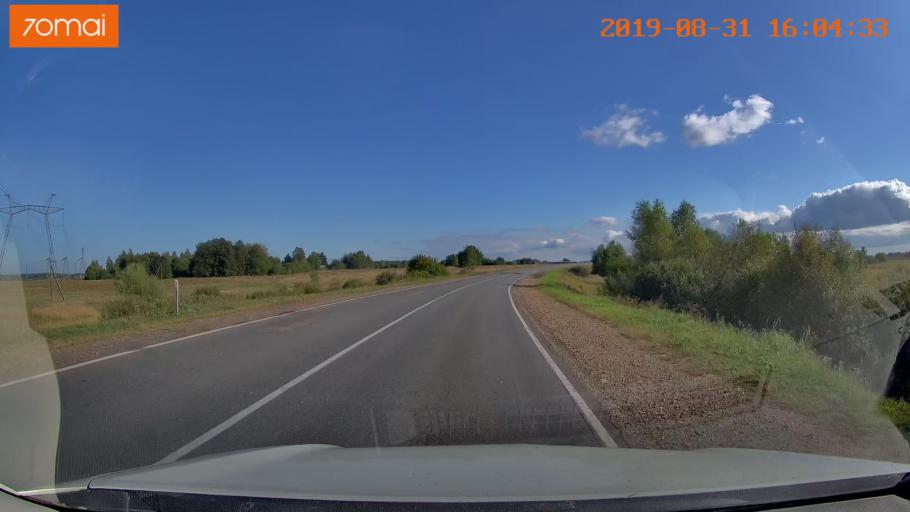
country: RU
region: Kaluga
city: Yukhnov
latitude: 54.6530
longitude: 35.3312
